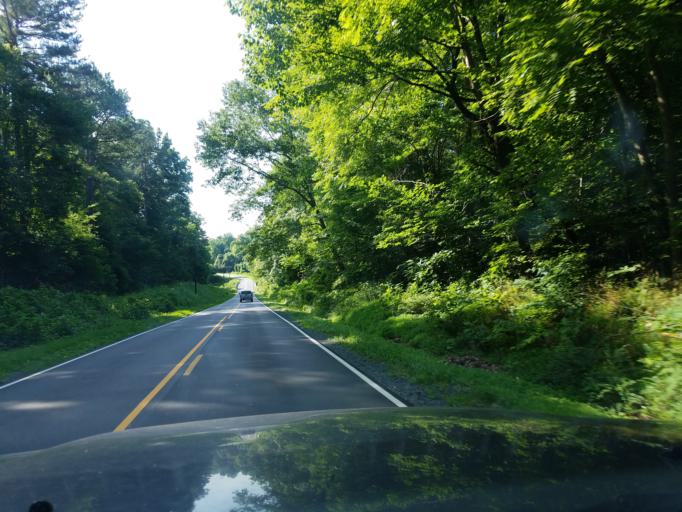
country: US
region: North Carolina
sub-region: Granville County
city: Butner
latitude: 36.1595
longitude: -78.7763
